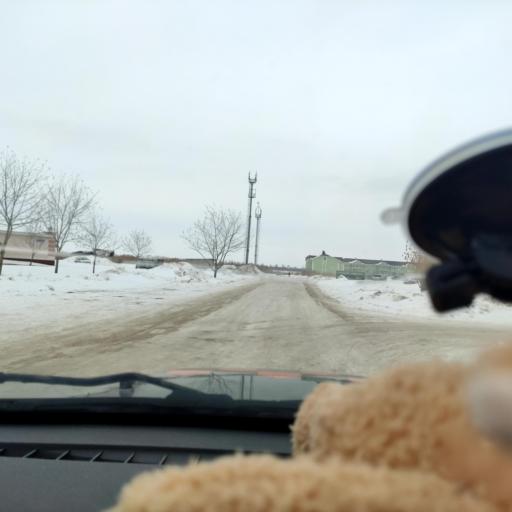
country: RU
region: Samara
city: Podstepki
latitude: 53.5287
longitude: 49.1806
